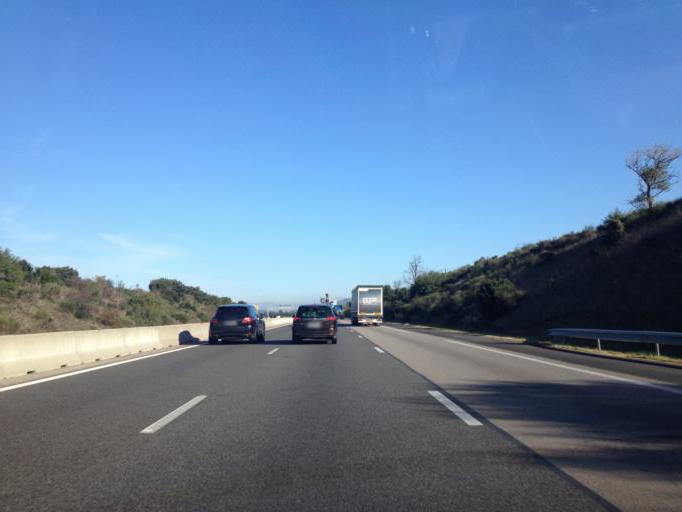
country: FR
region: Rhone-Alpes
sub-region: Departement de la Drome
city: Malataverne
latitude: 44.4655
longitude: 4.7626
